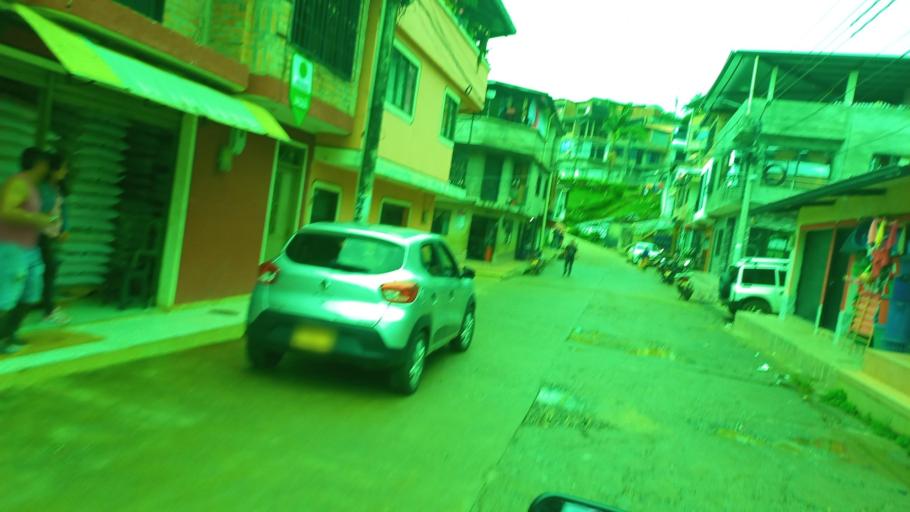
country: CO
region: Cauca
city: Balboa
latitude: 2.0390
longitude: -77.2181
